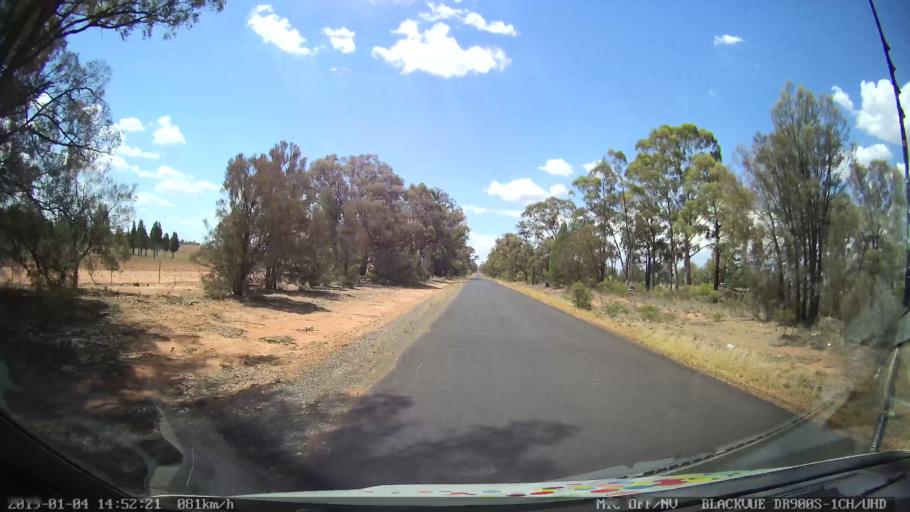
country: AU
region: New South Wales
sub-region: Dubbo Municipality
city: Dubbo
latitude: -32.0168
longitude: 148.6496
